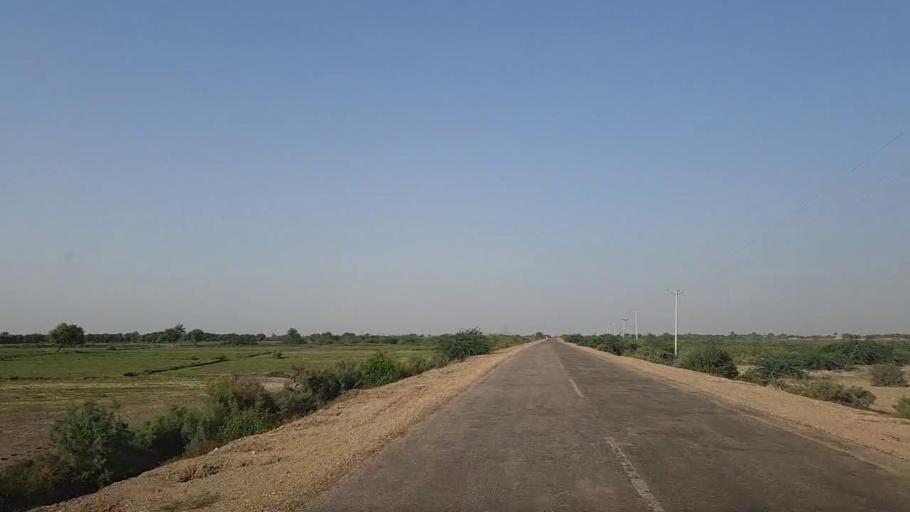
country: PK
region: Sindh
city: Mirpur Batoro
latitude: 24.6145
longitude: 68.4045
